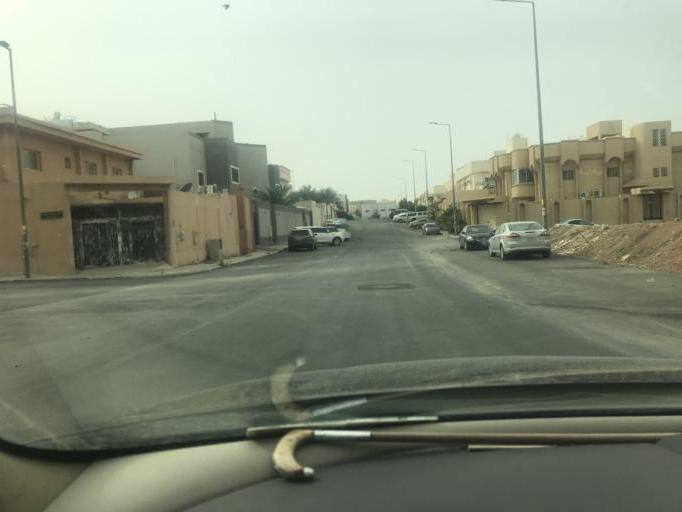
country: SA
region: Ar Riyad
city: Riyadh
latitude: 24.7336
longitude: 46.7630
